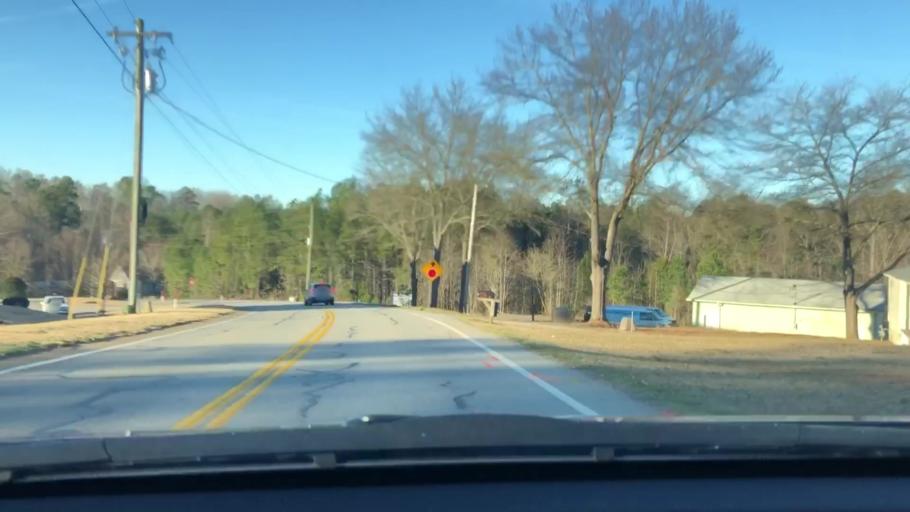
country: US
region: South Carolina
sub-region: Lexington County
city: Irmo
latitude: 34.0555
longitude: -81.1844
